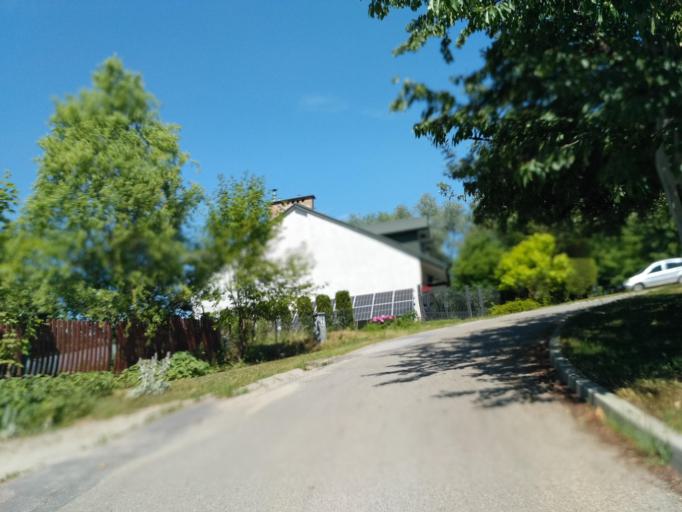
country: PL
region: Subcarpathian Voivodeship
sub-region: Krosno
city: Krosno
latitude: 49.7035
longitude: 21.7708
